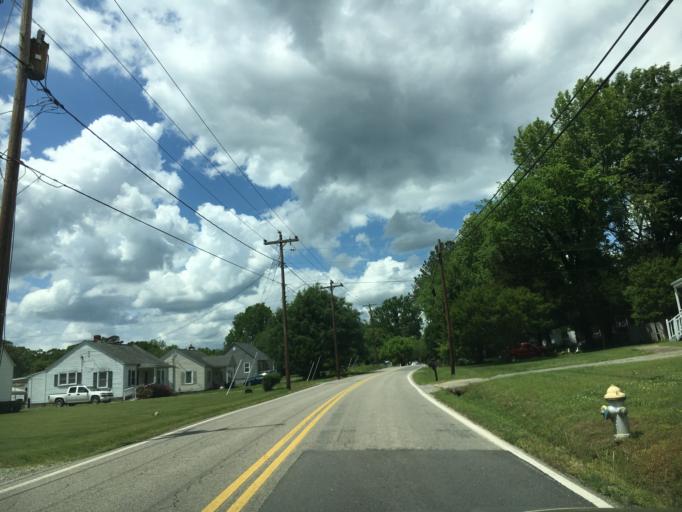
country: US
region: Virginia
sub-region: Halifax County
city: South Boston
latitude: 36.6998
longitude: -78.9236
